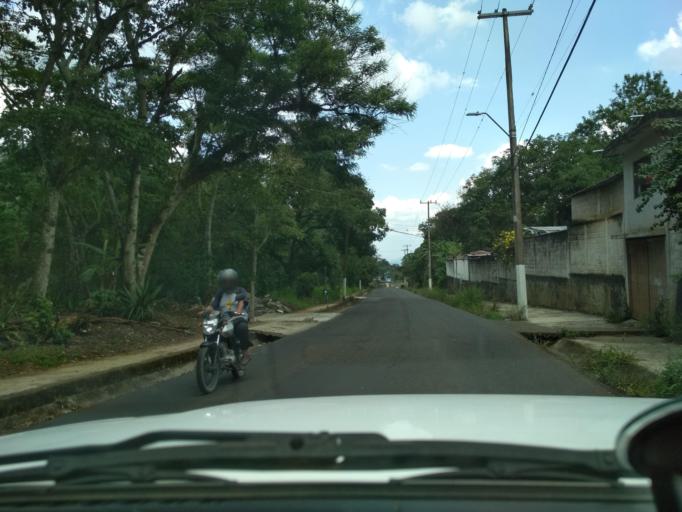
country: MX
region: Veracruz
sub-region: Cordoba
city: San Jose de Abajo [Unidad Habitacional]
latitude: 18.9197
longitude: -96.9618
